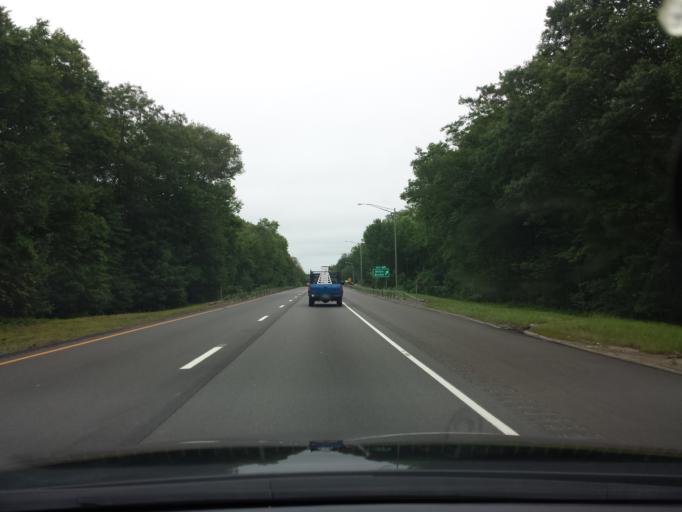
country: US
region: Connecticut
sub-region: New London County
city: Mystic
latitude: 41.3721
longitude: -71.9885
